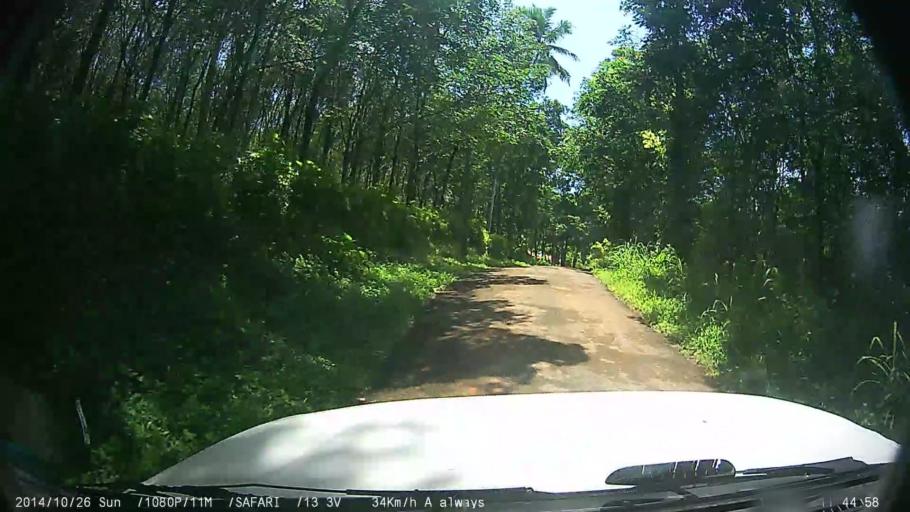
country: IN
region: Kerala
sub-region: Kottayam
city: Palackattumala
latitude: 9.7821
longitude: 76.5607
